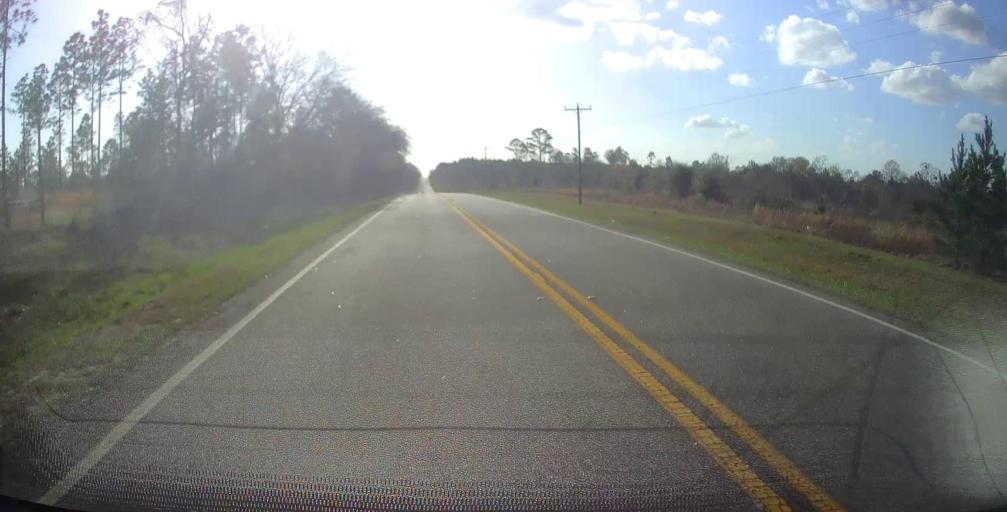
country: US
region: Georgia
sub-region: Wheeler County
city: Alamo
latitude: 32.1710
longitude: -82.6909
